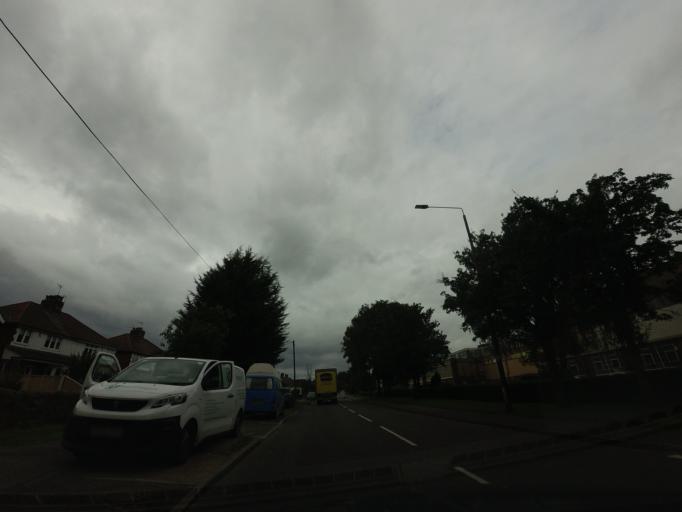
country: GB
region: England
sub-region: Nottinghamshire
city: Kimberley
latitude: 53.0013
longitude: -1.2469
